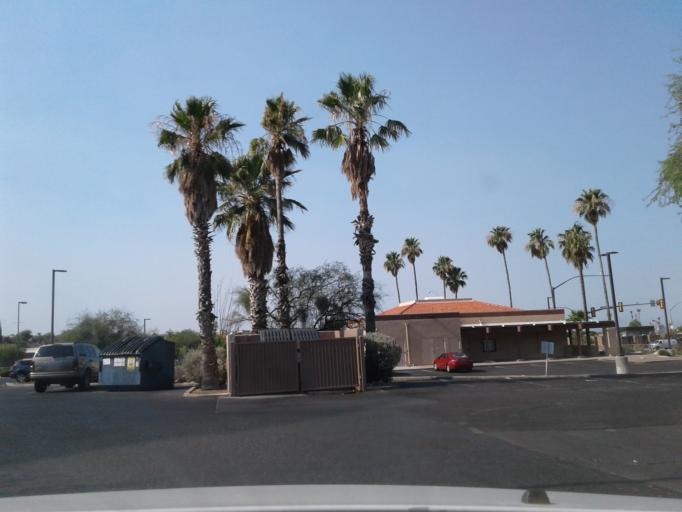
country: US
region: Arizona
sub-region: Pima County
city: Catalina Foothills
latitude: 32.3095
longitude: -110.8919
